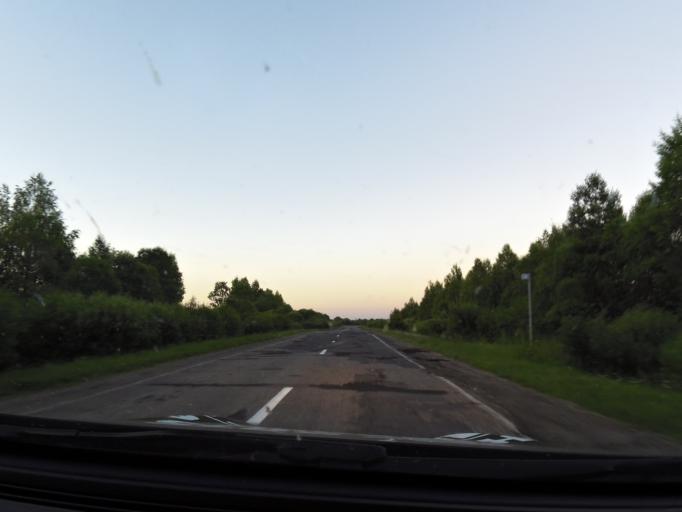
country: RU
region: Jaroslavl
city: Lyubim
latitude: 58.3395
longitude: 41.0934
